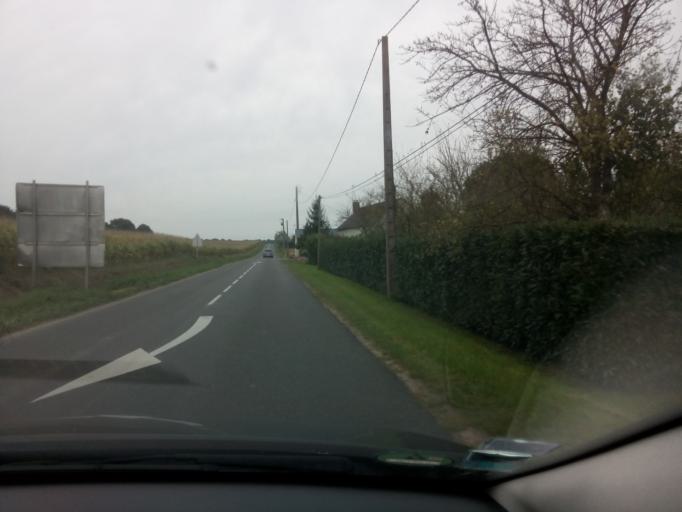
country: FR
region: Pays de la Loire
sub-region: Departement de Maine-et-Loire
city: Seiches-sur-le-Loir
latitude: 47.5692
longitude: -0.3454
